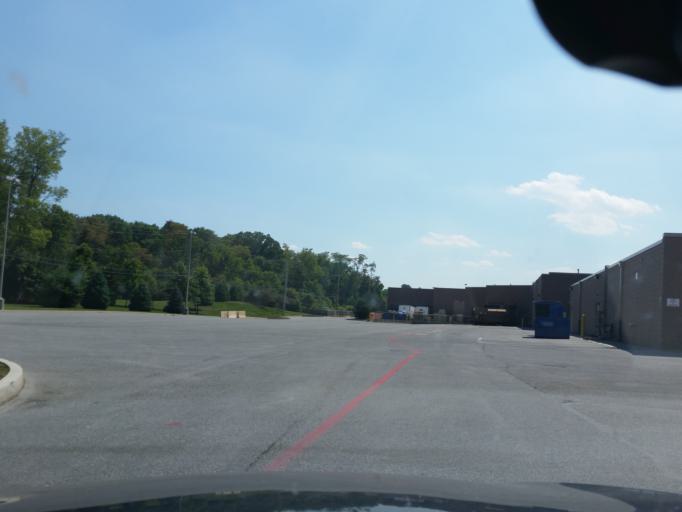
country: US
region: Pennsylvania
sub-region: Cumberland County
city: Carlisle
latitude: 40.1974
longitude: -77.1552
